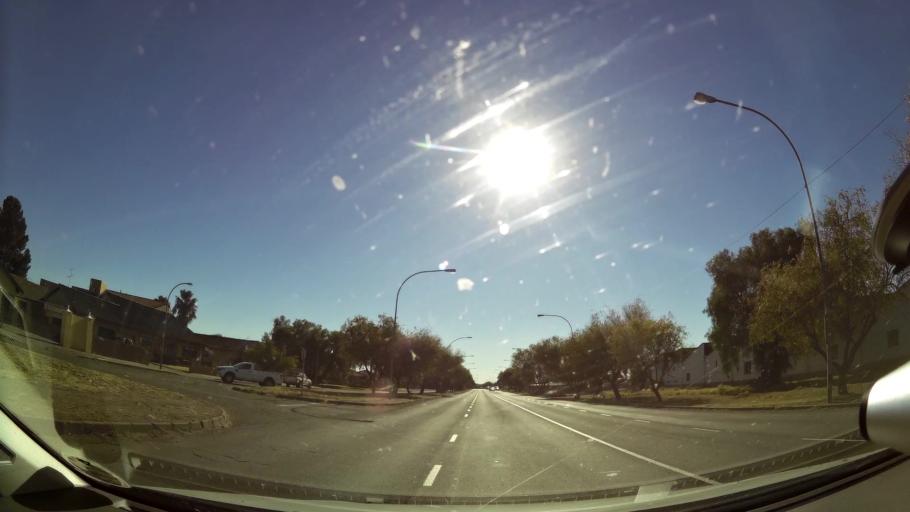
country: ZA
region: Northern Cape
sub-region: Frances Baard District Municipality
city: Kimberley
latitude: -28.7224
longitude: 24.7714
